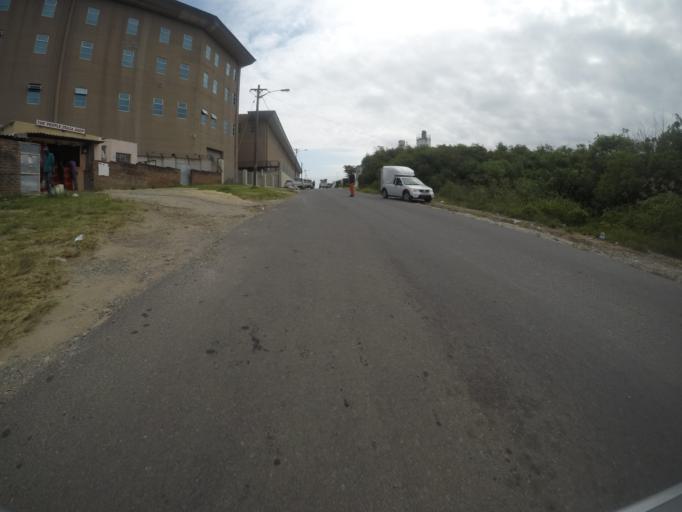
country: ZA
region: Eastern Cape
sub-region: Buffalo City Metropolitan Municipality
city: East London
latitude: -32.9842
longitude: 27.8921
